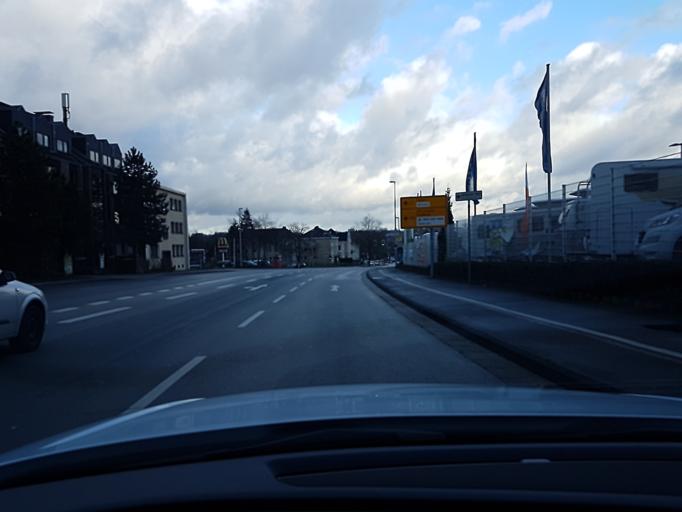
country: DE
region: North Rhine-Westphalia
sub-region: Regierungsbezirk Dusseldorf
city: Muelheim (Ruhr)
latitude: 51.3993
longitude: 6.8763
